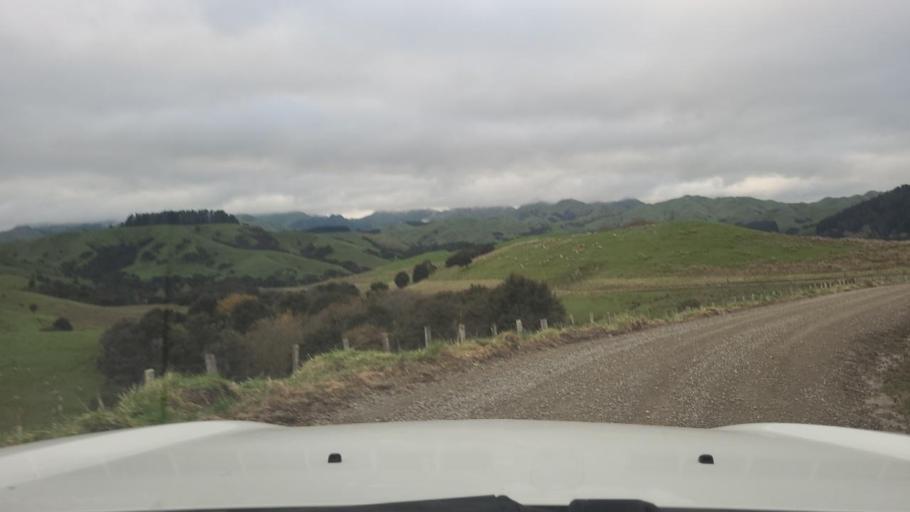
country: NZ
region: Wellington
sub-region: Masterton District
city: Masterton
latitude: -41.1644
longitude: 175.6919
